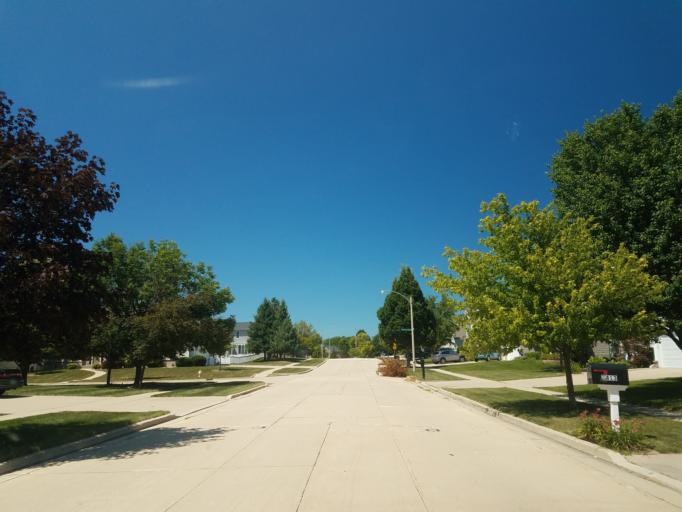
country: US
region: Illinois
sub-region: McLean County
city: Normal
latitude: 40.5009
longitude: -88.9139
